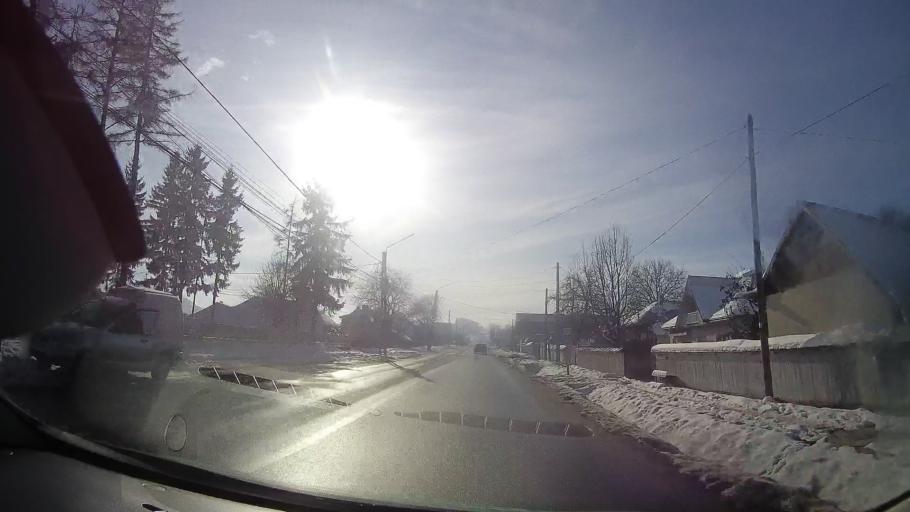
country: RO
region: Neamt
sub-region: Oras Targu Neamt
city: Humulesti
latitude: 47.1949
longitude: 26.3466
